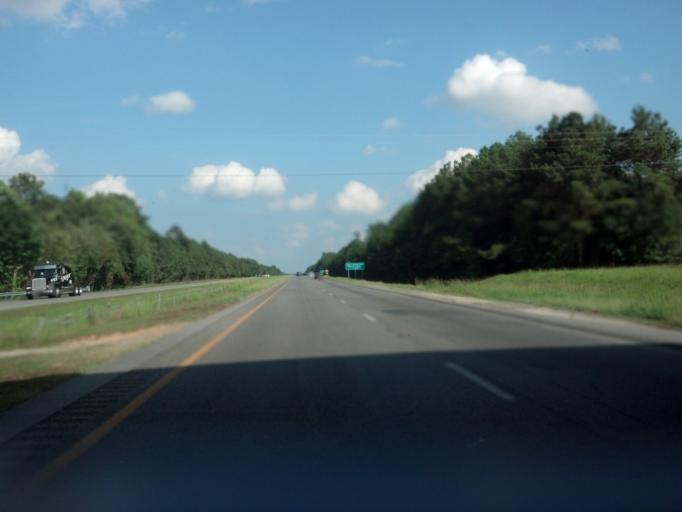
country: US
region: North Carolina
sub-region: Nash County
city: Rocky Mount
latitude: 35.9327
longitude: -77.7100
